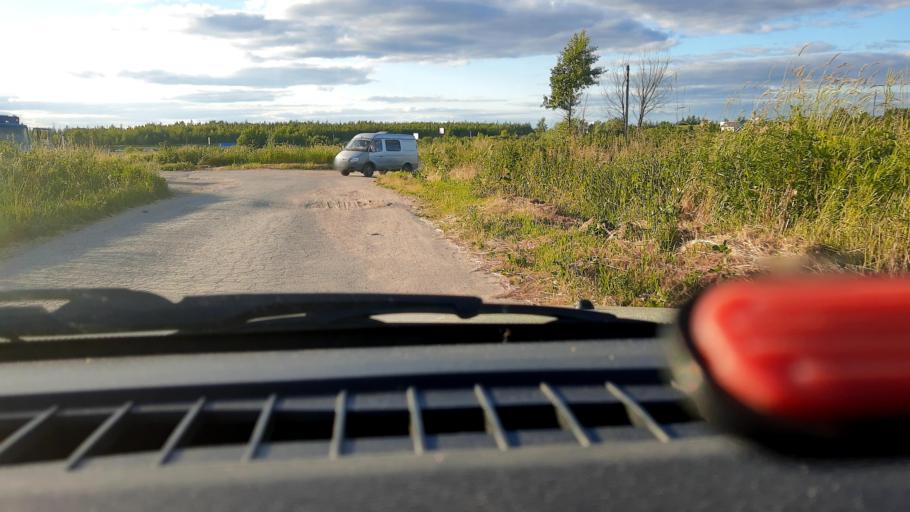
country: RU
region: Nizjnij Novgorod
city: Burevestnik
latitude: 56.1984
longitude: 43.8577
